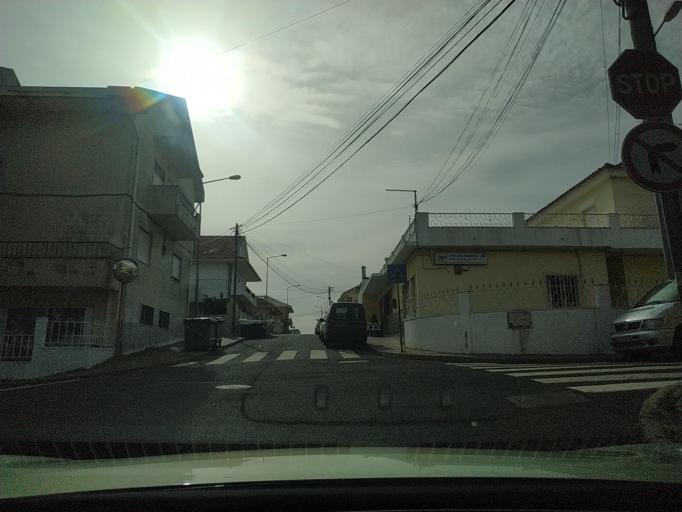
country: PT
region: Lisbon
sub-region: Amadora
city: Amadora
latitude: 38.7749
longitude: -9.2371
